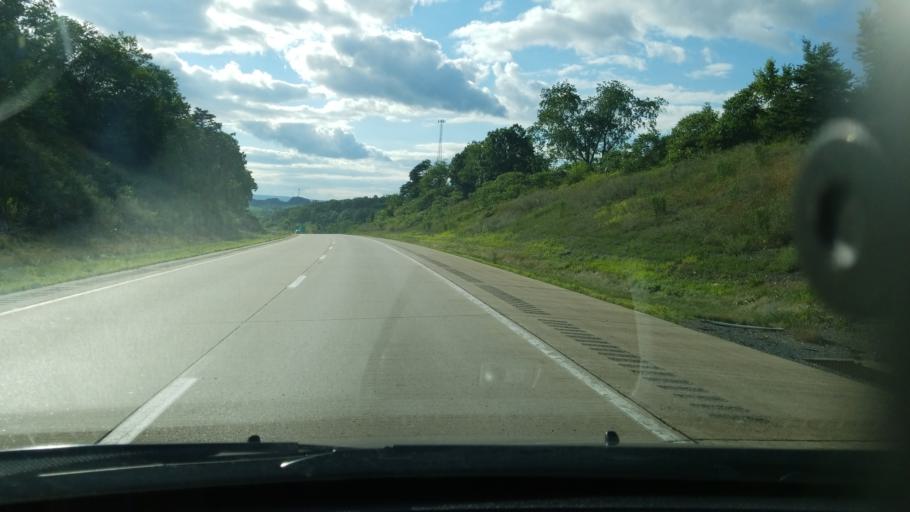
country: US
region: Pennsylvania
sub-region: Northumberland County
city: Milton
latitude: 41.0026
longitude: -76.7519
